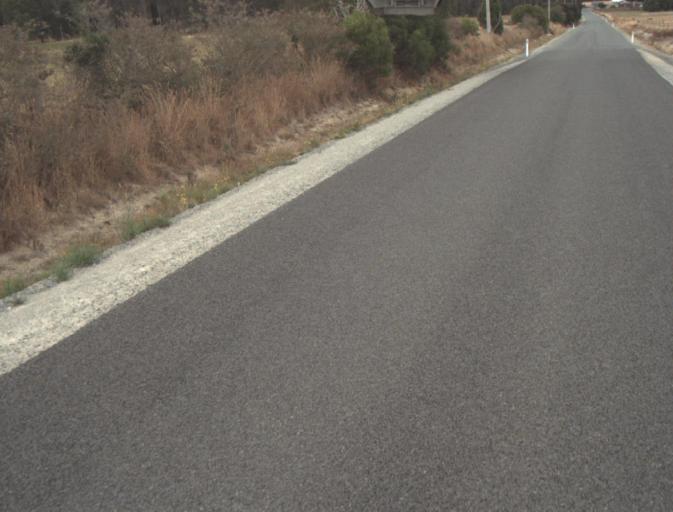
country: AU
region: Tasmania
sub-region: Launceston
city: Mayfield
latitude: -41.2018
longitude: 147.1893
